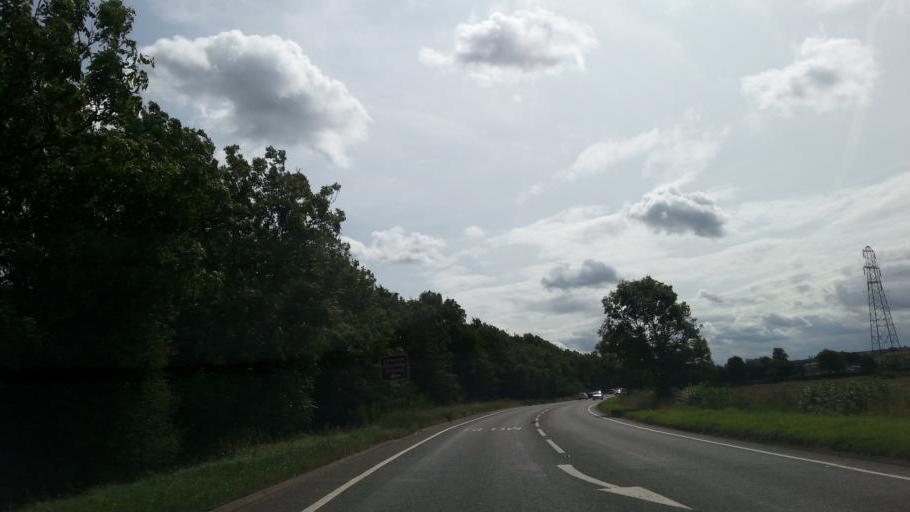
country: GB
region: England
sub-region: Leicestershire
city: Kibworth Harcourt
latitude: 52.5300
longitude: -0.9683
